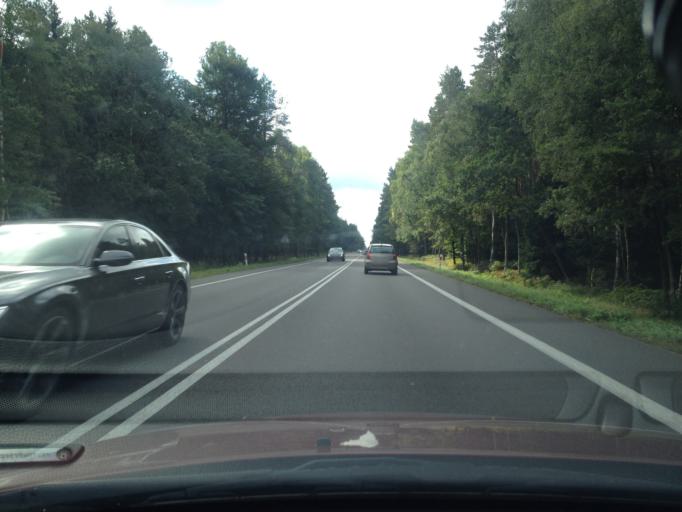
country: PL
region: West Pomeranian Voivodeship
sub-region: Powiat goleniowski
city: Goleniow
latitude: 53.6582
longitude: 14.8154
